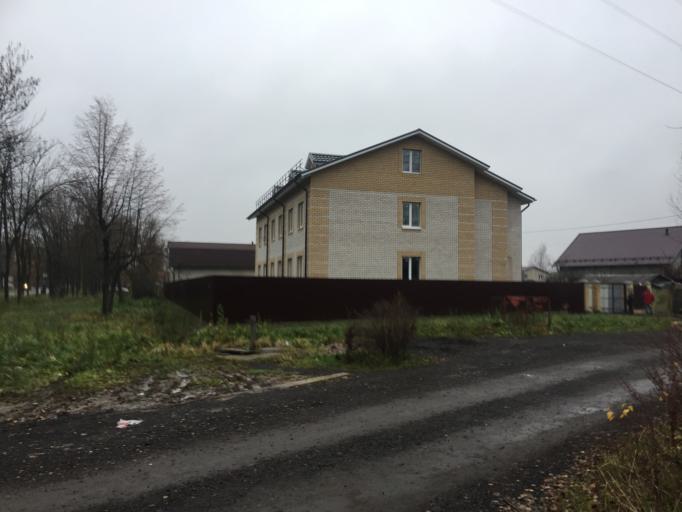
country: RU
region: Jaroslavl
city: Yaroslavl
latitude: 57.7172
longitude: 39.7669
